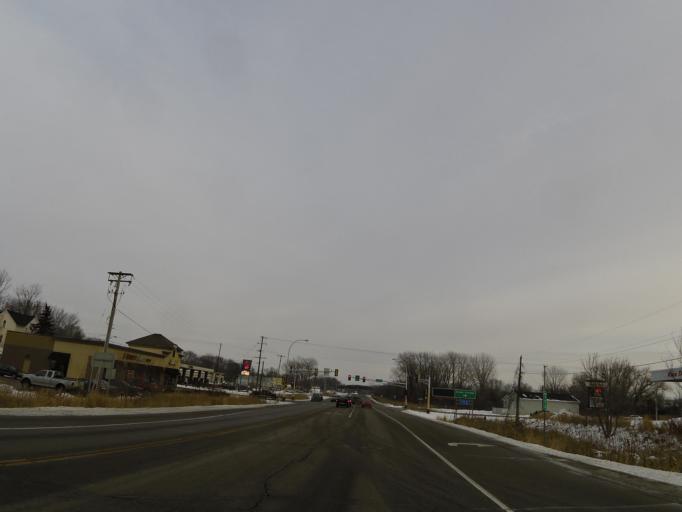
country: US
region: Minnesota
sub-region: Hennepin County
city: Saint Bonifacius
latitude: 44.9018
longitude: -93.7488
